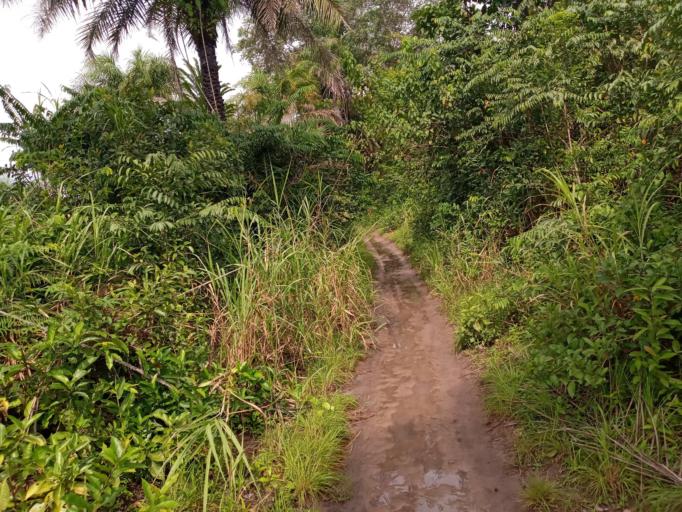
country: SL
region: Southern Province
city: Bonthe
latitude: 7.5177
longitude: -12.5418
